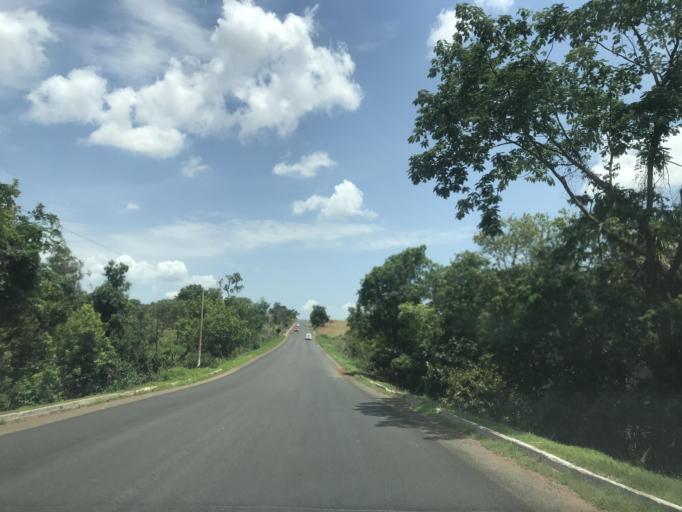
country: BR
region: Goias
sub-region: Bela Vista De Goias
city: Bela Vista de Goias
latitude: -17.0796
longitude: -48.6570
